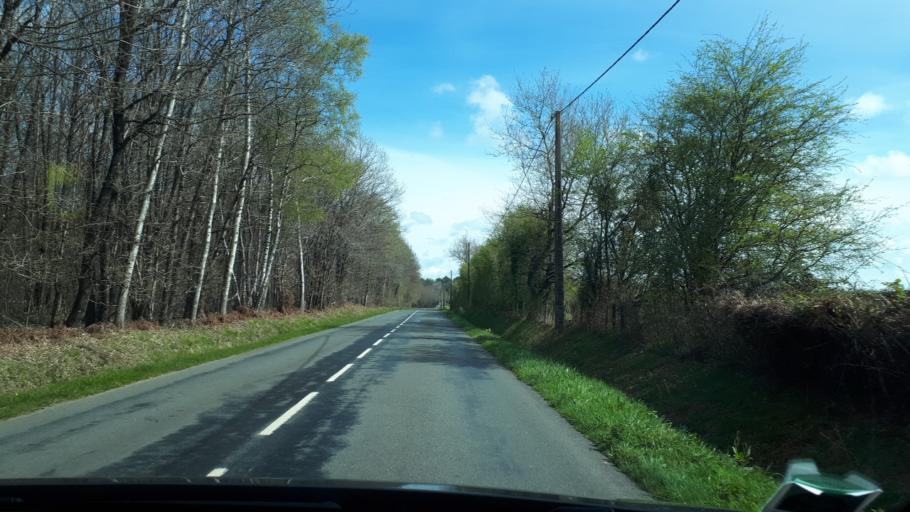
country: FR
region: Pays de la Loire
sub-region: Departement de la Sarthe
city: Le Grand-Luce
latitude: 47.8806
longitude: 0.5299
